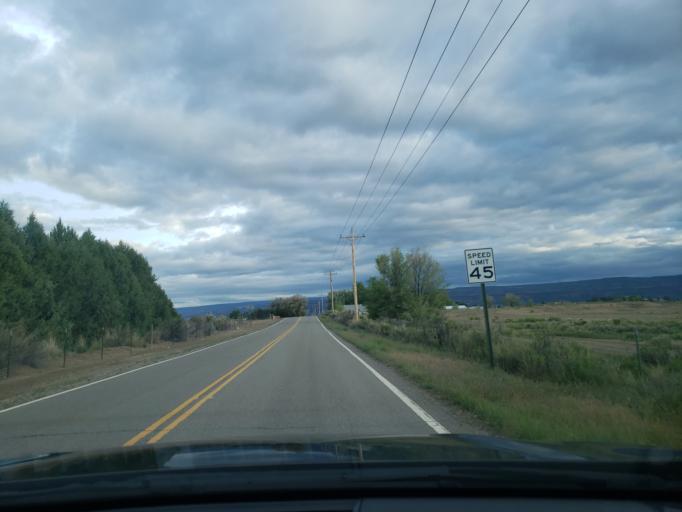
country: US
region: Colorado
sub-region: Mesa County
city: Fruita
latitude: 39.2215
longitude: -108.7011
